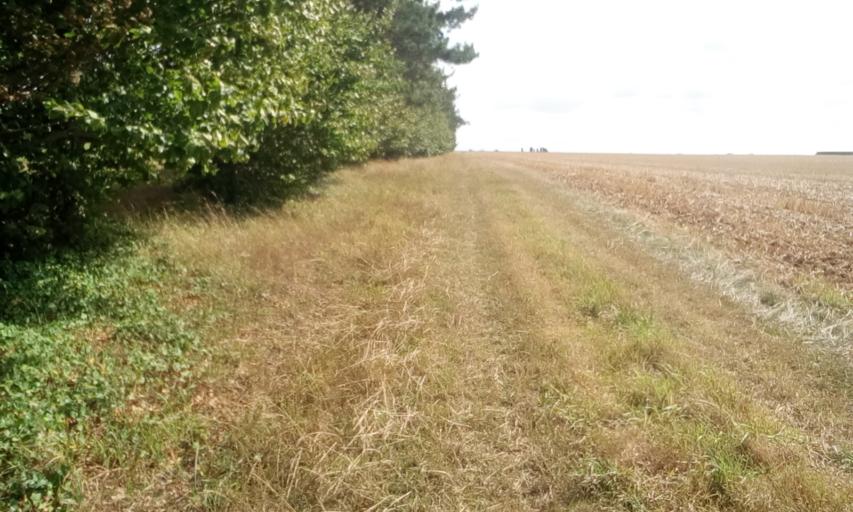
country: FR
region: Lower Normandy
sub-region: Departement du Calvados
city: Saint-Sylvain
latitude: 49.0802
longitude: -0.1982
